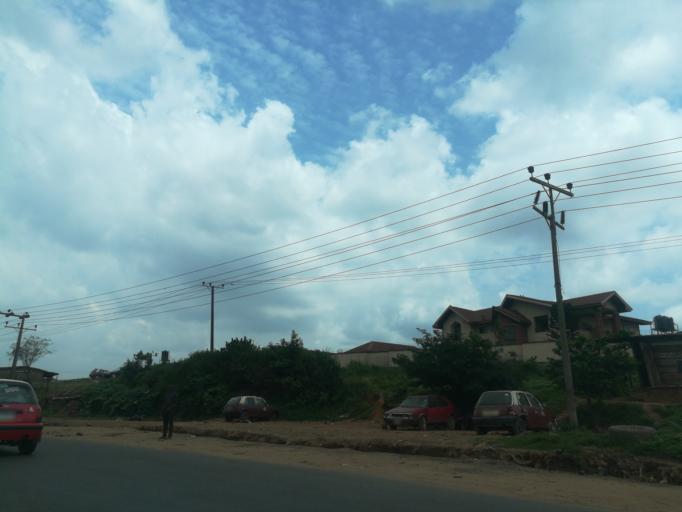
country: NG
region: Oyo
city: Ibadan
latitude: 7.4156
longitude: 3.9425
